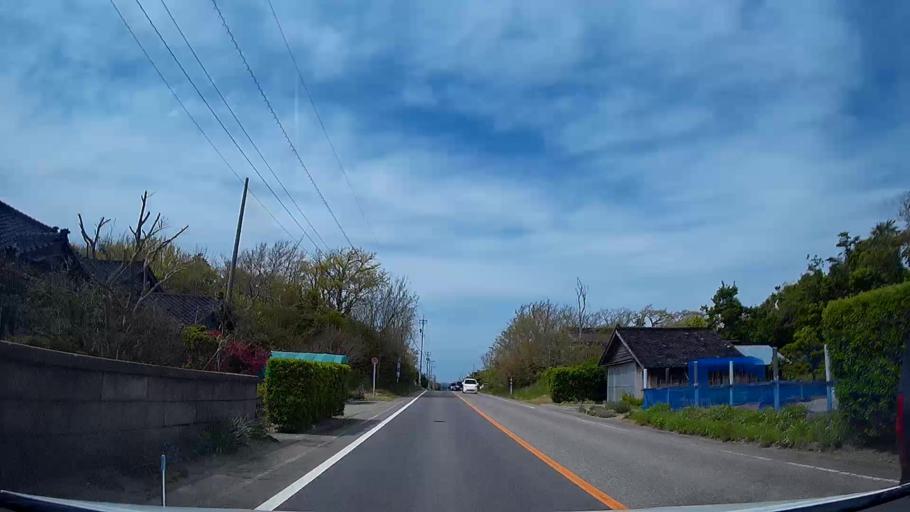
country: JP
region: Ishikawa
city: Hakui
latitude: 36.9646
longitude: 136.7731
